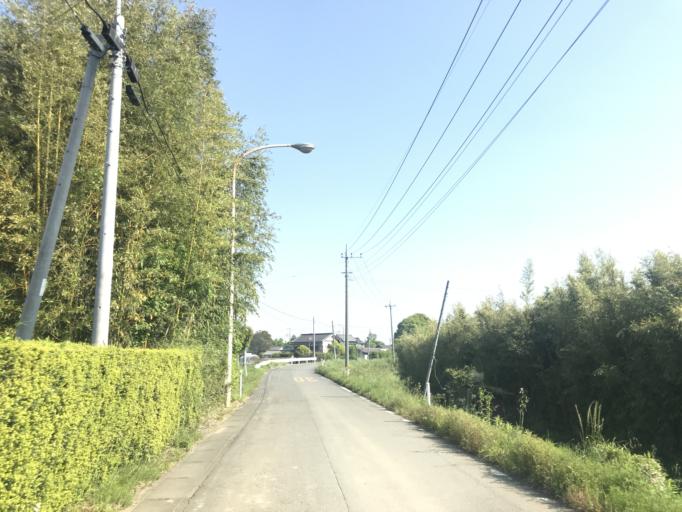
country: JP
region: Ibaraki
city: Mitsukaido
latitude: 36.0559
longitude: 140.0149
